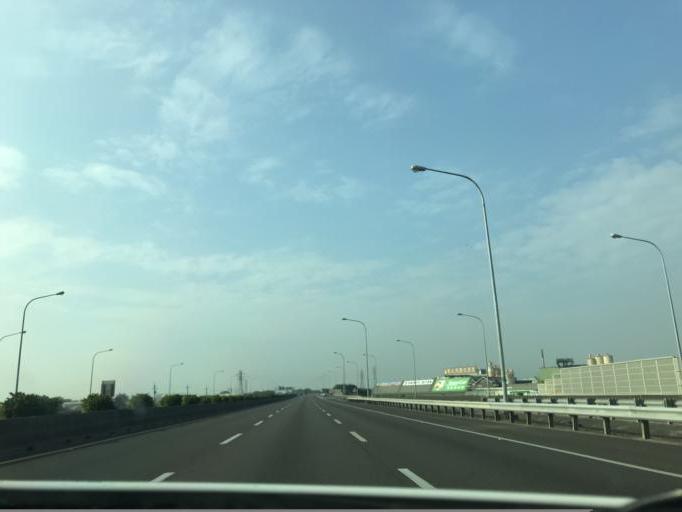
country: TW
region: Taiwan
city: Xinying
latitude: 23.3051
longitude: 120.2891
